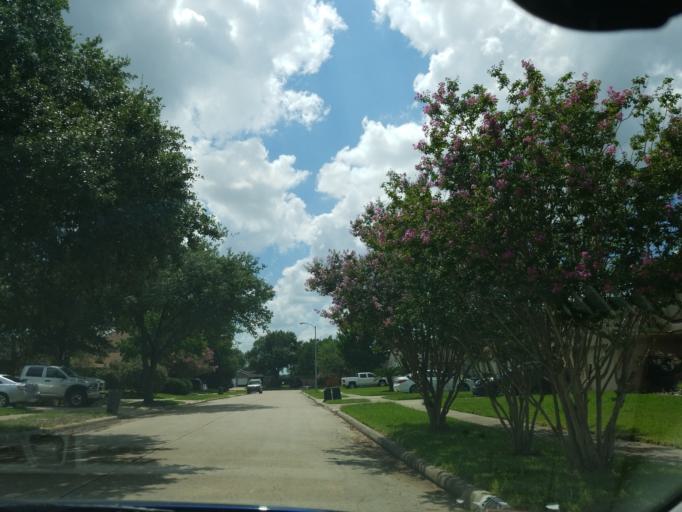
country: US
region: Texas
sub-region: Harris County
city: Cypress
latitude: 29.8744
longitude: -95.7331
